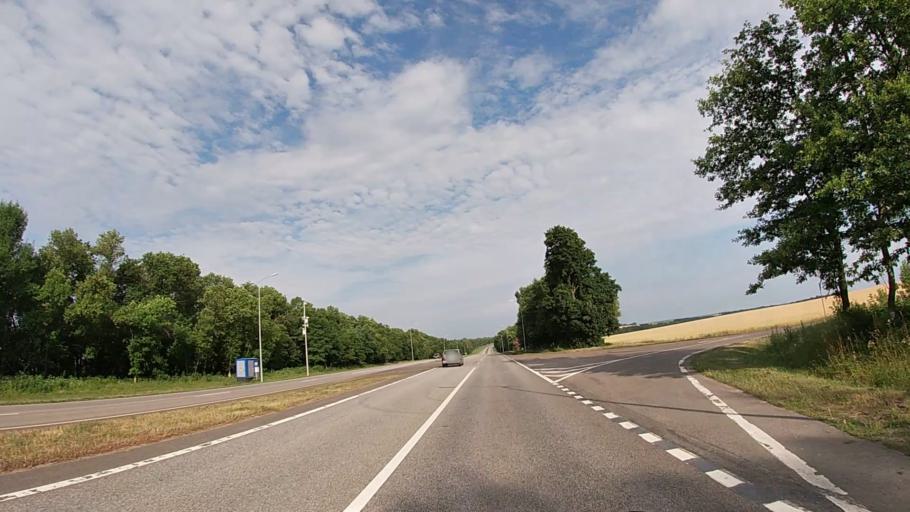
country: RU
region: Belgorod
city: Tomarovka
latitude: 50.6642
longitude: 36.3255
